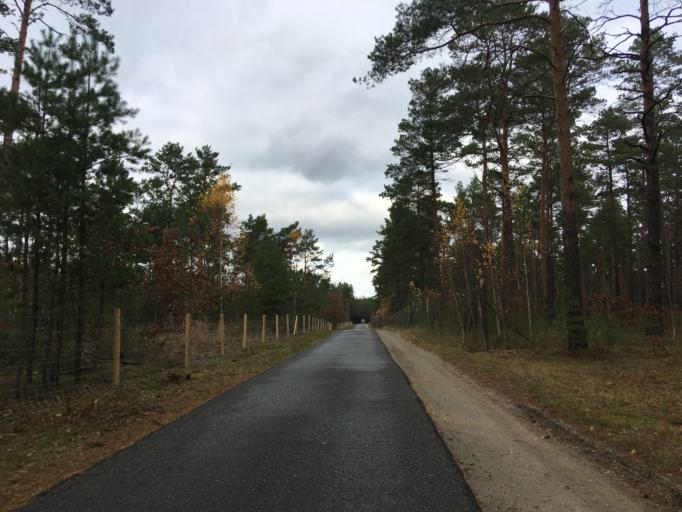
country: DE
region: Brandenburg
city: Tauer
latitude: 51.9915
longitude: 14.5157
